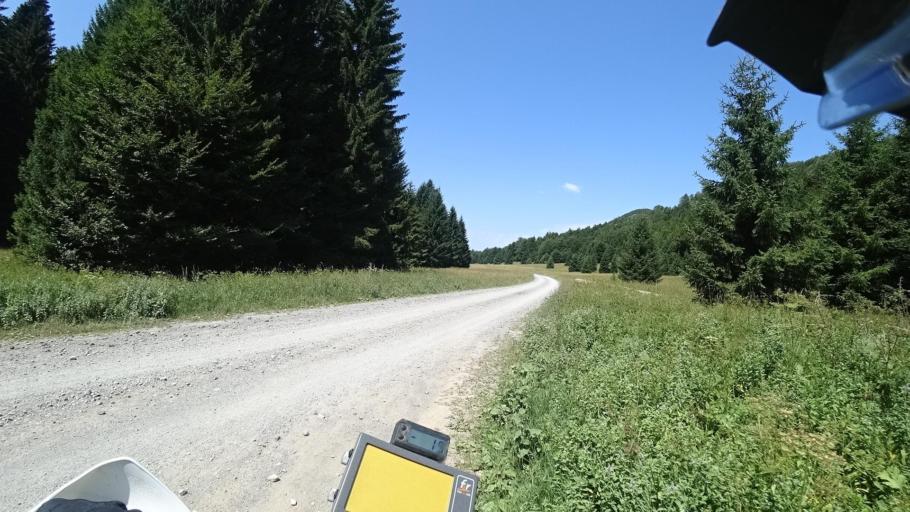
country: HR
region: Primorsko-Goranska
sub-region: Grad Delnice
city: Delnice
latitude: 45.2737
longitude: 14.9150
